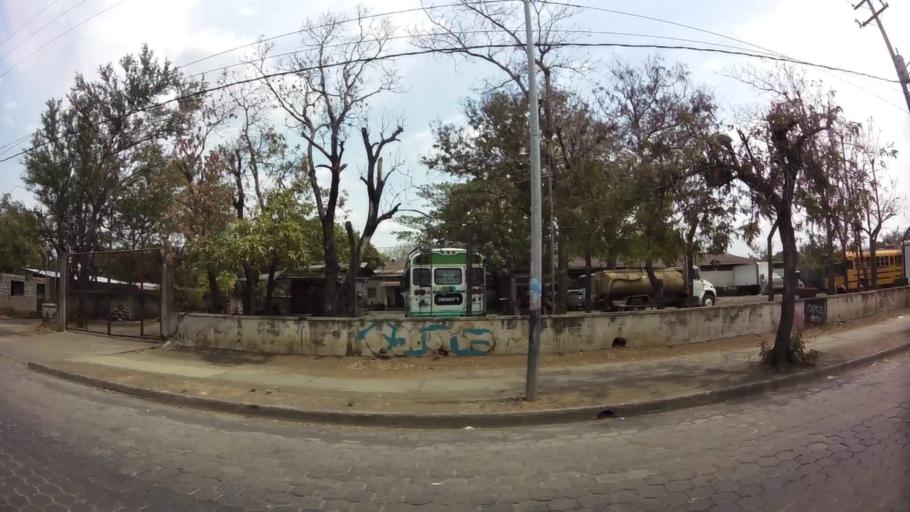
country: NI
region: Managua
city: Ciudad Sandino
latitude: 12.1578
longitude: -86.2956
